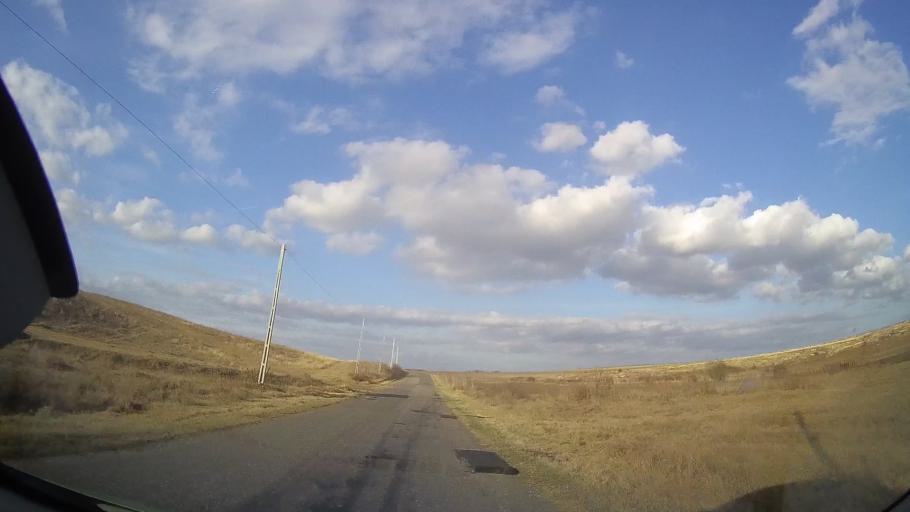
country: RO
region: Constanta
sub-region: Comuna Cerchezu
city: Cerchezu
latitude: 43.8407
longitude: 28.0980
